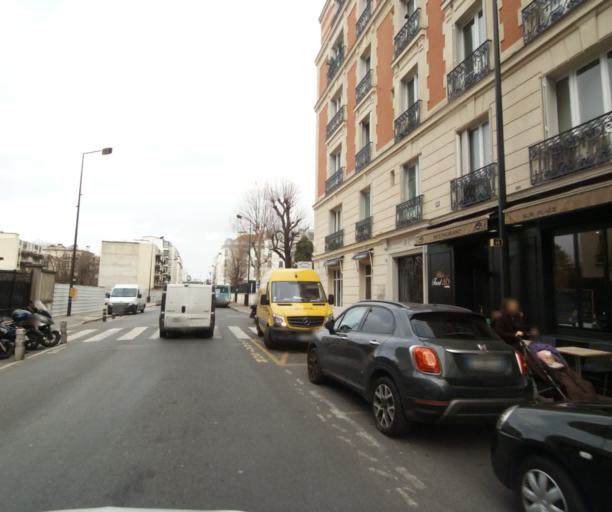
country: FR
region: Ile-de-France
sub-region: Departement des Hauts-de-Seine
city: Levallois-Perret
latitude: 48.8895
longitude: 2.2804
